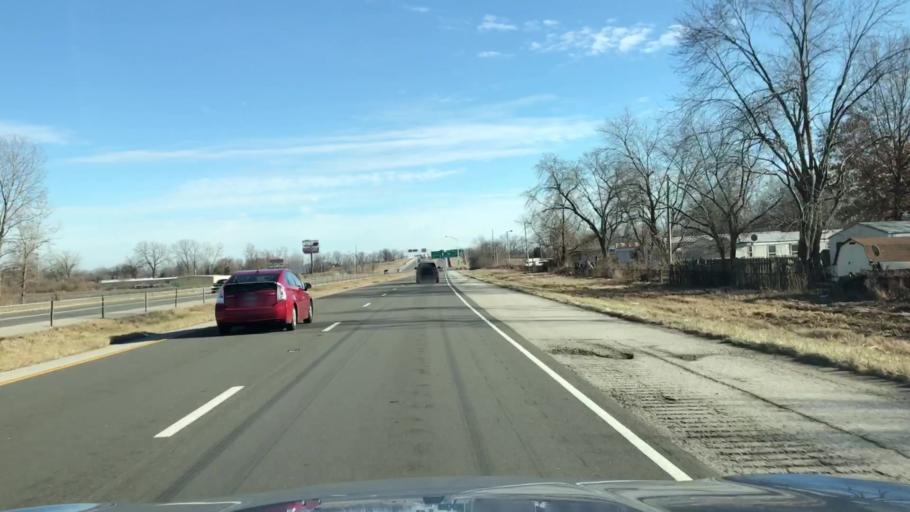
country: US
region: Illinois
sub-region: Madison County
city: Mitchell
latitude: 38.7635
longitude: -90.1054
